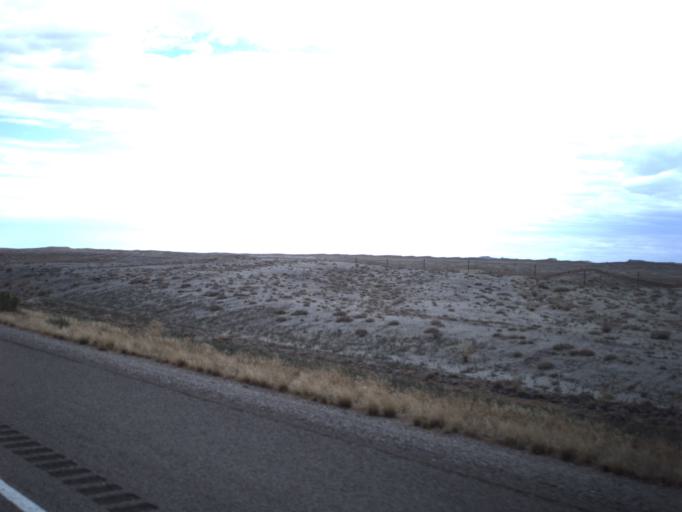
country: US
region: Utah
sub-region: Grand County
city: Moab
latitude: 38.9349
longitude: -110.0248
